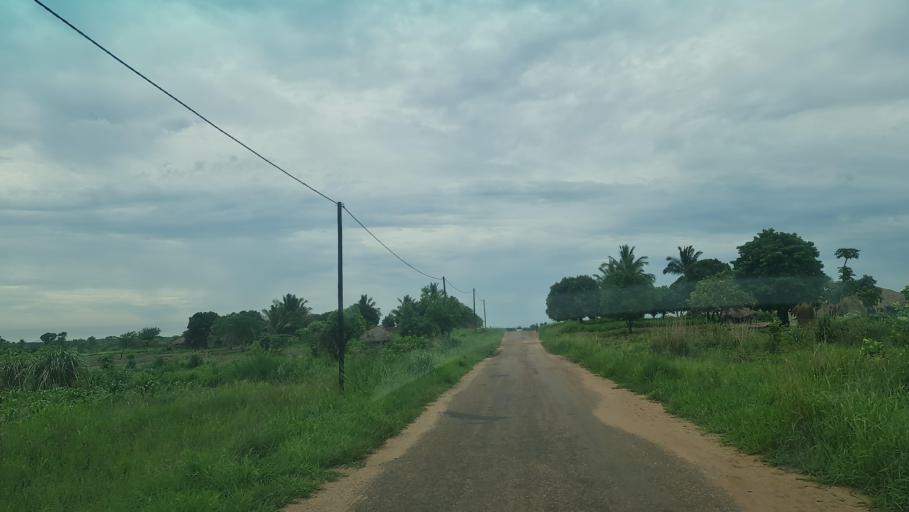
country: MW
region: Southern Region
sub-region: Nsanje District
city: Nsanje
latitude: -17.6765
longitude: 35.7210
